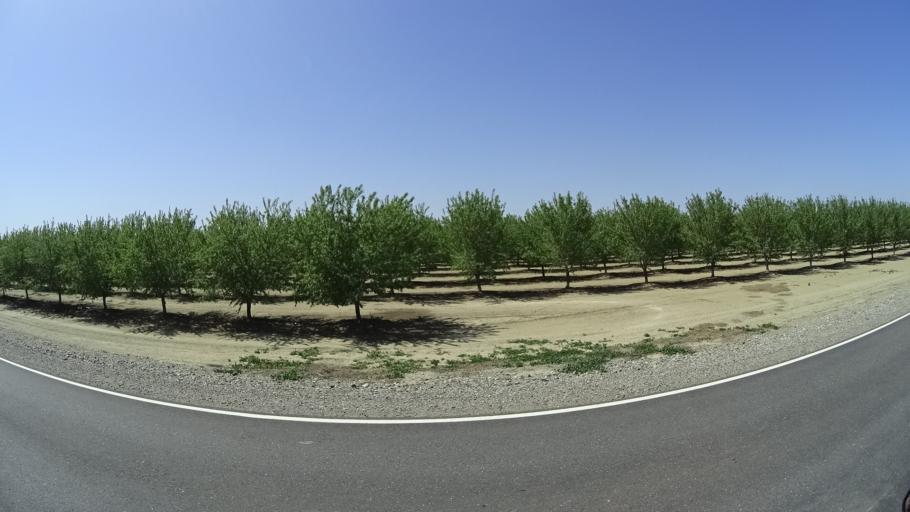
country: US
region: California
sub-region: Glenn County
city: Willows
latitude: 39.5995
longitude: -122.1374
